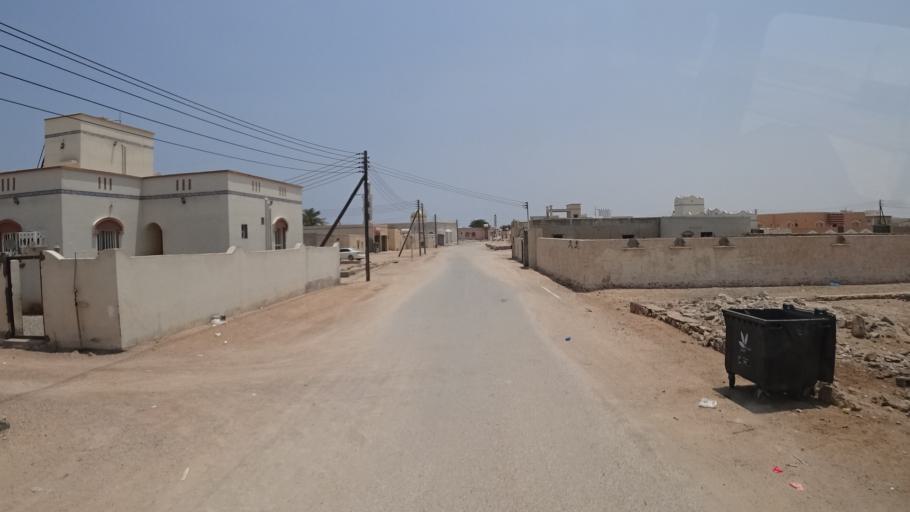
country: OM
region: Ash Sharqiyah
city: Sur
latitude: 22.5168
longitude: 59.7989
